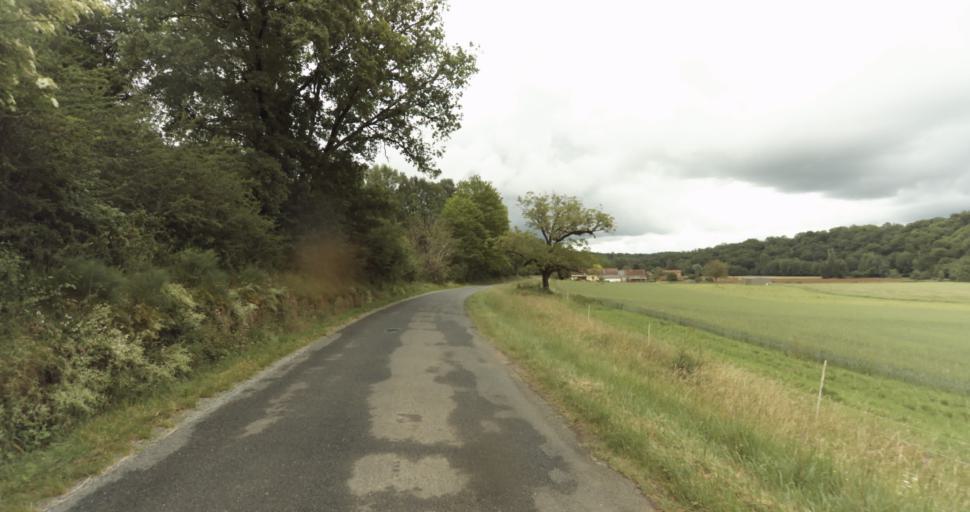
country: FR
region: Aquitaine
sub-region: Departement de la Dordogne
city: Belves
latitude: 44.7588
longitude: 0.8903
